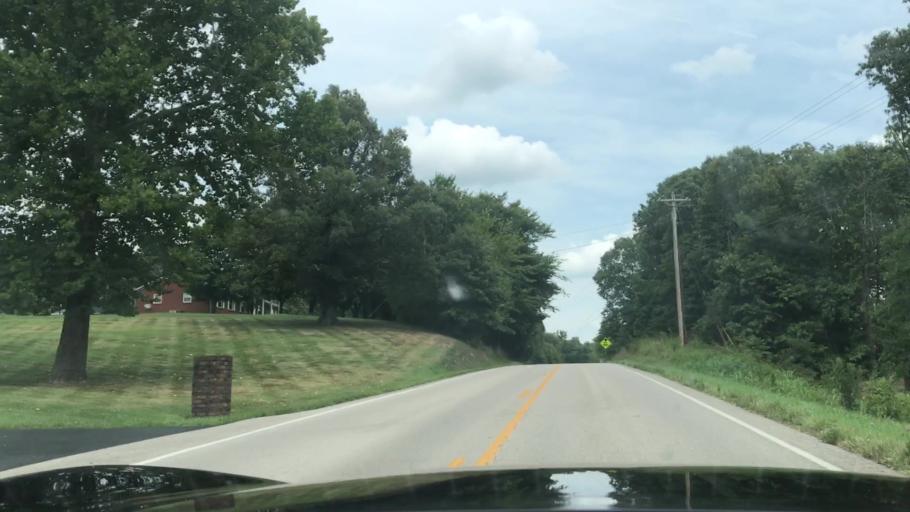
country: US
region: Kentucky
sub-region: Butler County
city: Morgantown
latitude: 37.1873
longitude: -86.7618
